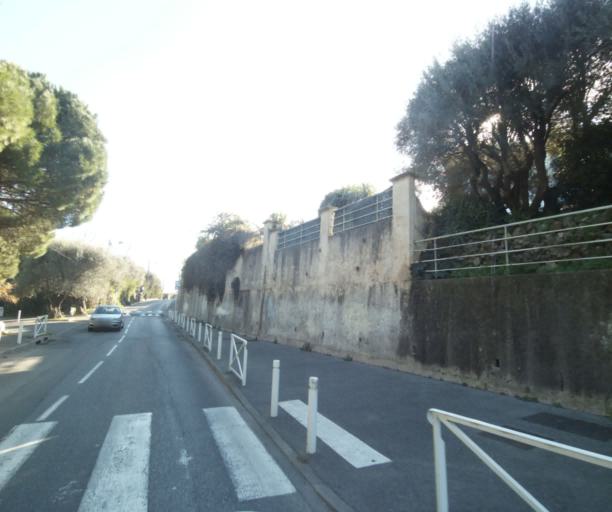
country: FR
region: Provence-Alpes-Cote d'Azur
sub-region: Departement des Alpes-Maritimes
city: Biot
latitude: 43.5990
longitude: 7.1069
